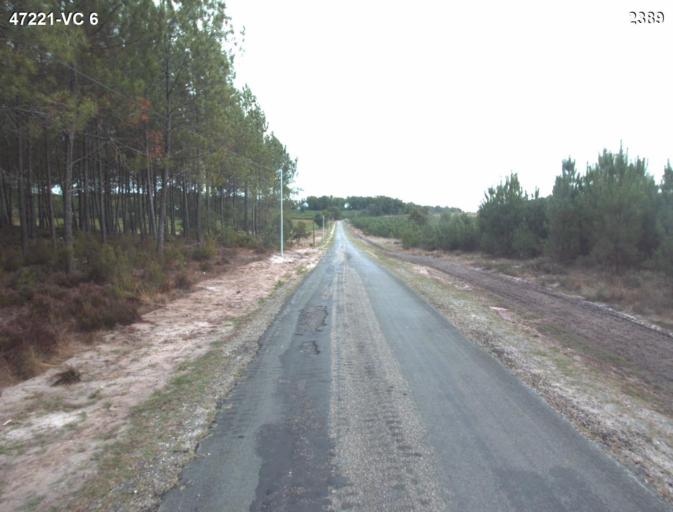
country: FR
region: Aquitaine
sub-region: Departement du Lot-et-Garonne
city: Mezin
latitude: 44.1067
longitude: 0.1538
